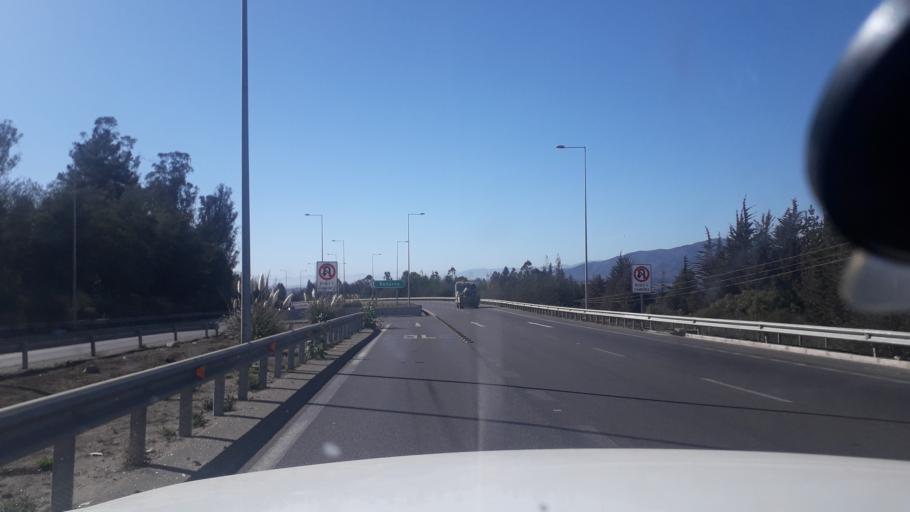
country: CL
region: Valparaiso
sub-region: Provincia de Valparaiso
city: Vina del Mar
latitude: -32.9553
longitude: -71.5095
